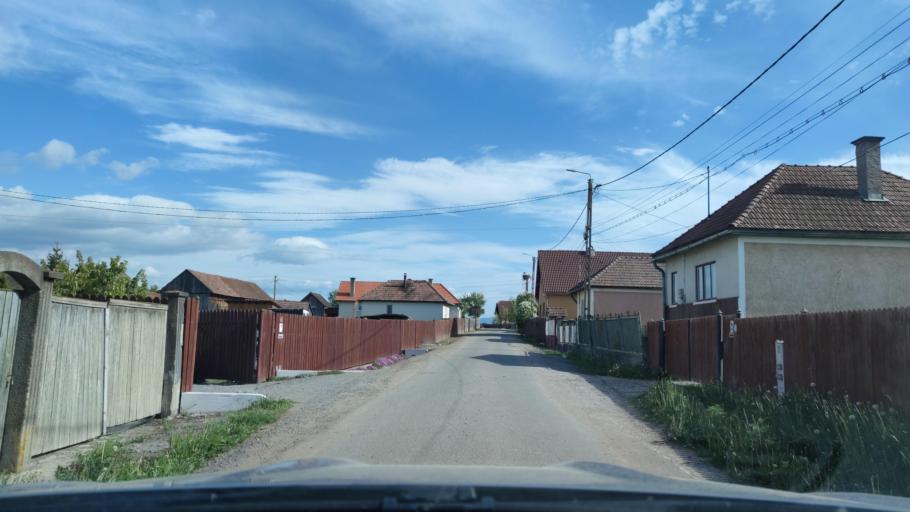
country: RO
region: Harghita
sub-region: Comuna Ditrau
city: Ditrau
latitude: 46.7957
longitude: 25.4880
